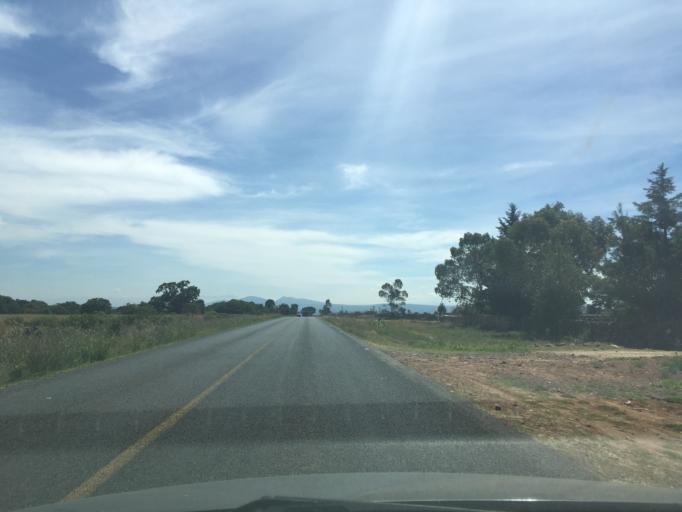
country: MX
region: Queretaro
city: Amealco
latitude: 20.2131
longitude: -100.1065
